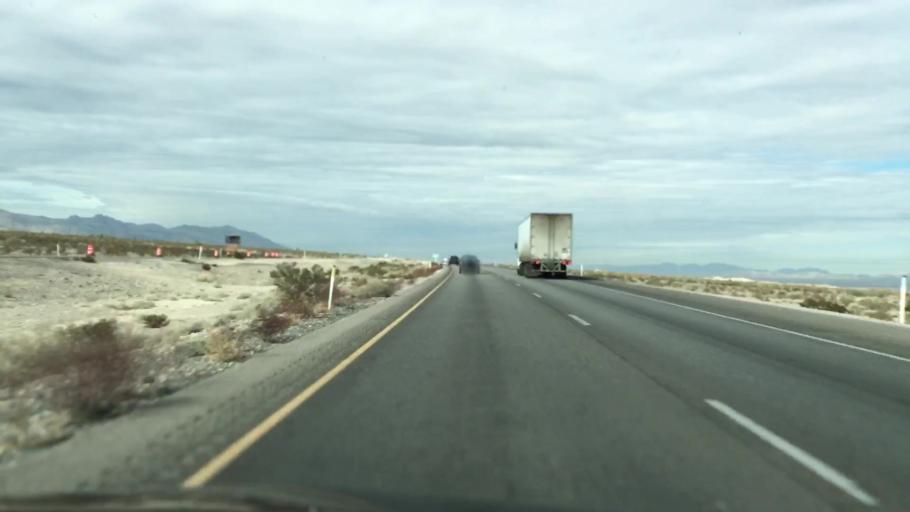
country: US
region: Nevada
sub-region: Clark County
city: Summerlin South
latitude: 36.3376
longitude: -115.3215
